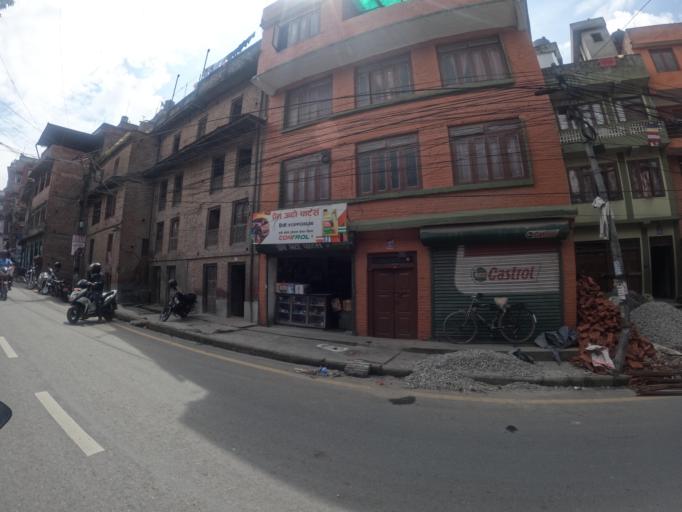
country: NP
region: Central Region
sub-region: Bagmati Zone
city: Bhaktapur
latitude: 27.6824
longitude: 85.3828
